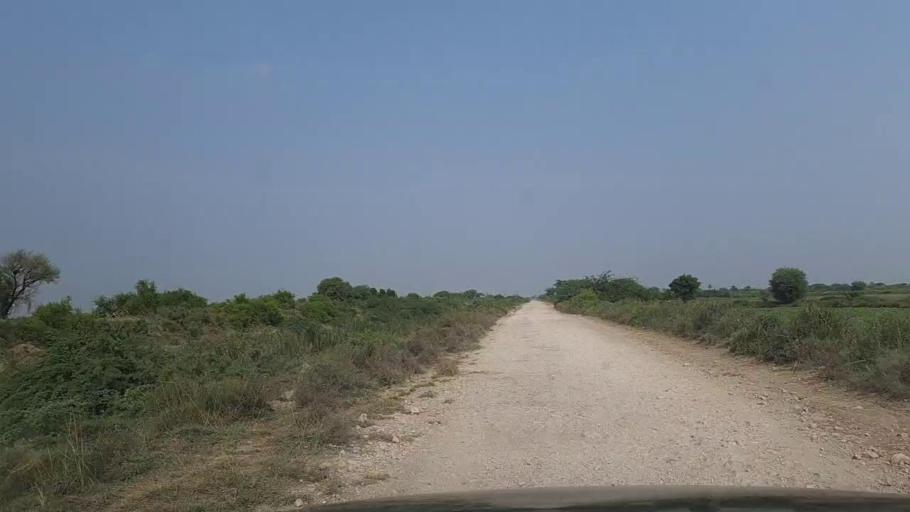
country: PK
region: Sindh
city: Thatta
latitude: 24.7450
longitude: 67.8068
